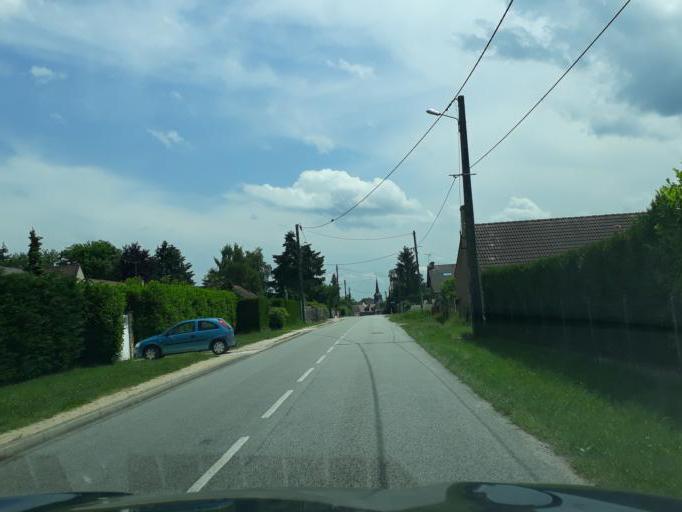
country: FR
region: Centre
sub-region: Departement du Loiret
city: Tigy
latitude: 47.7139
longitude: 2.2080
